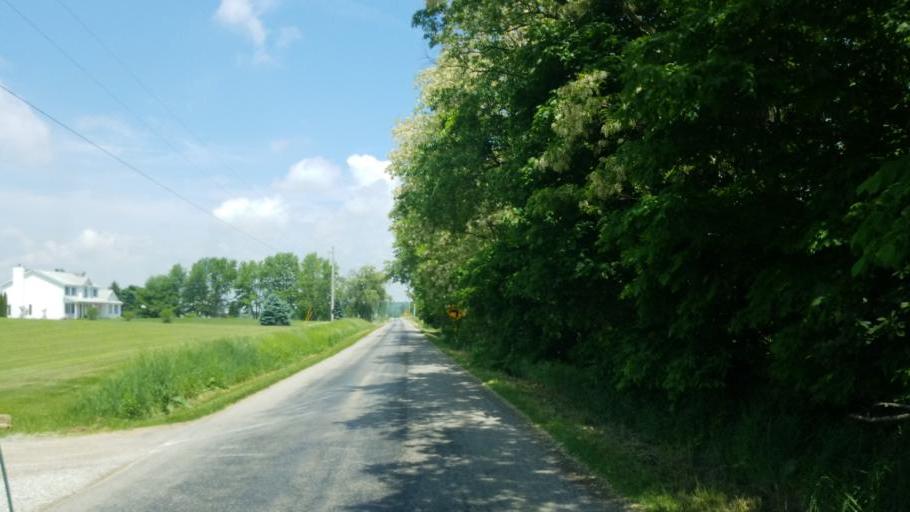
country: US
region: Ohio
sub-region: Ashland County
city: Ashland
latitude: 40.8376
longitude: -82.2535
